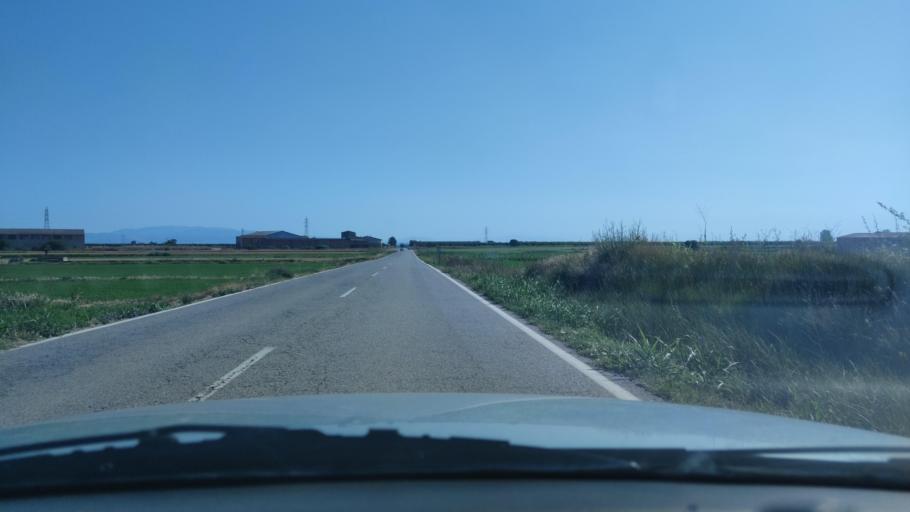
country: ES
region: Catalonia
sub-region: Provincia de Lleida
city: Bellvis
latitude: 41.6454
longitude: 0.7966
